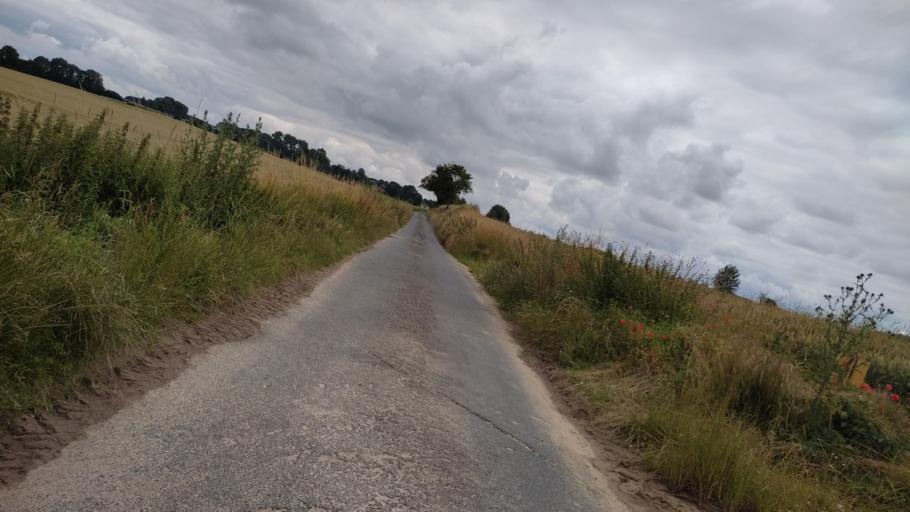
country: FR
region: Nord-Pas-de-Calais
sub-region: Departement du Pas-de-Calais
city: Beaumetz-les-Loges
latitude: 50.2486
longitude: 2.6377
